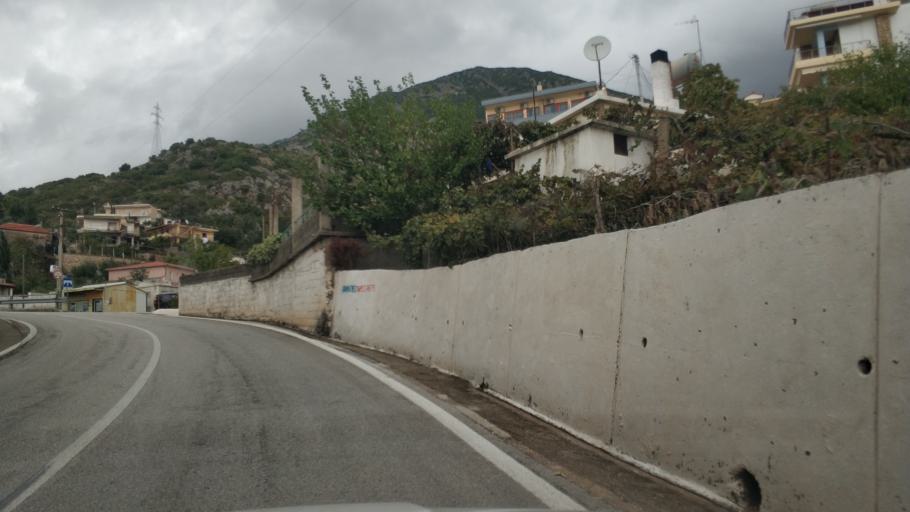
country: AL
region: Vlore
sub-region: Rrethi i Vlores
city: Vranisht
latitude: 40.1560
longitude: 19.6333
